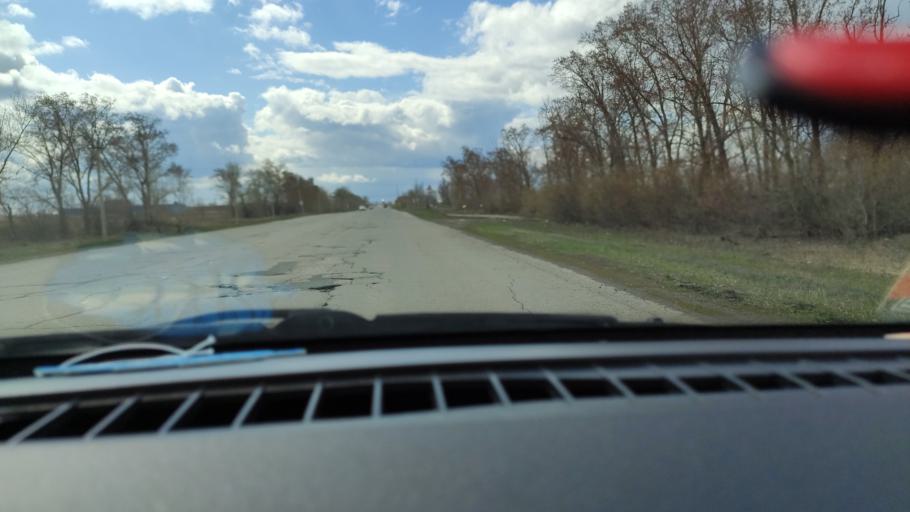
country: RU
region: Samara
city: Tol'yatti
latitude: 53.5862
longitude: 49.4050
